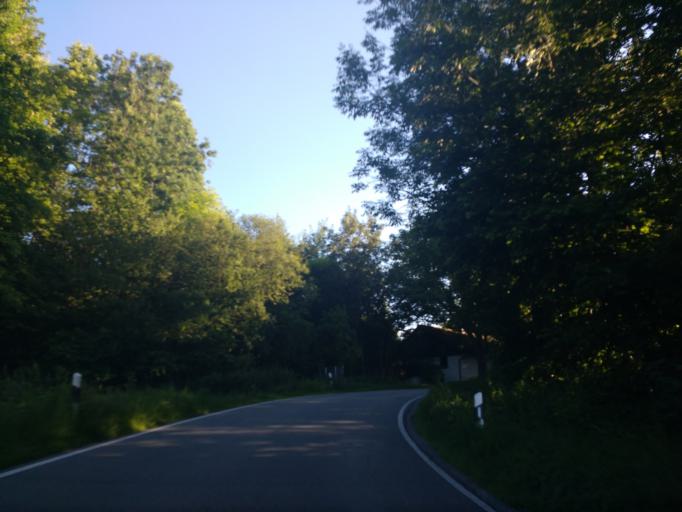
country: DE
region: Bavaria
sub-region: Upper Bavaria
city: Oberneukirchen
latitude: 48.1981
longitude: 12.4923
